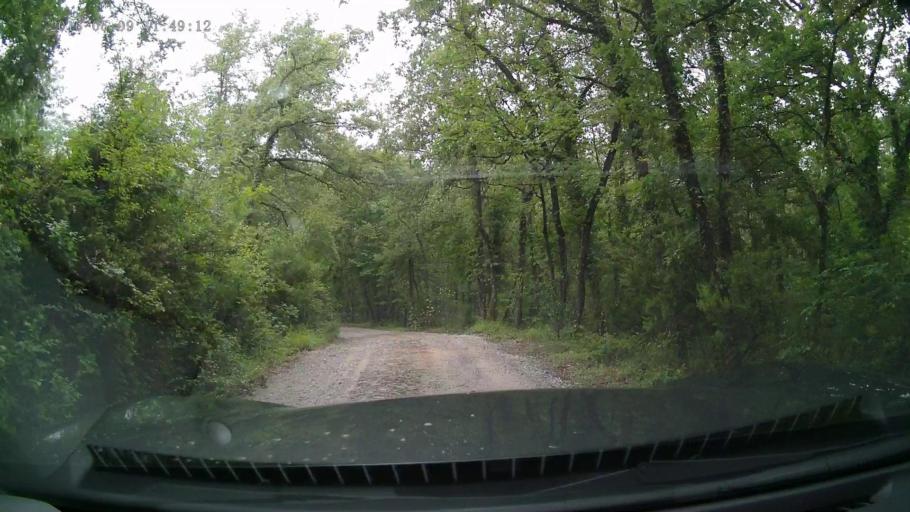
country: IT
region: Tuscany
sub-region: Province of Florence
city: Greve in Chianti
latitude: 43.5684
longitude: 11.2994
